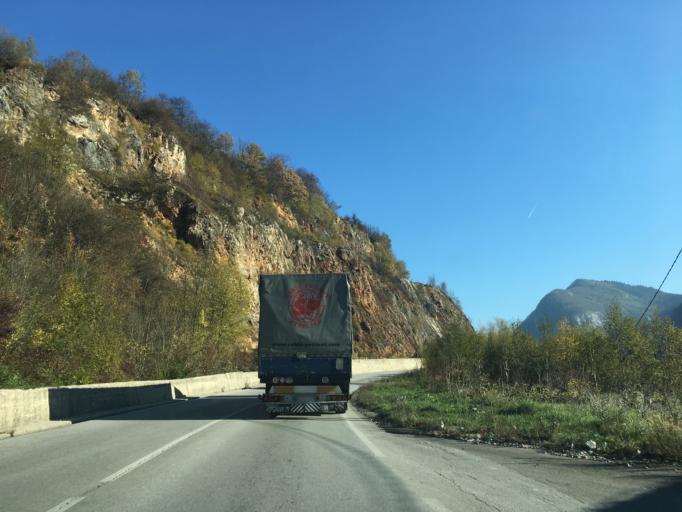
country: BA
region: Federation of Bosnia and Herzegovina
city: Kobilja Glava
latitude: 43.8439
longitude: 18.4767
